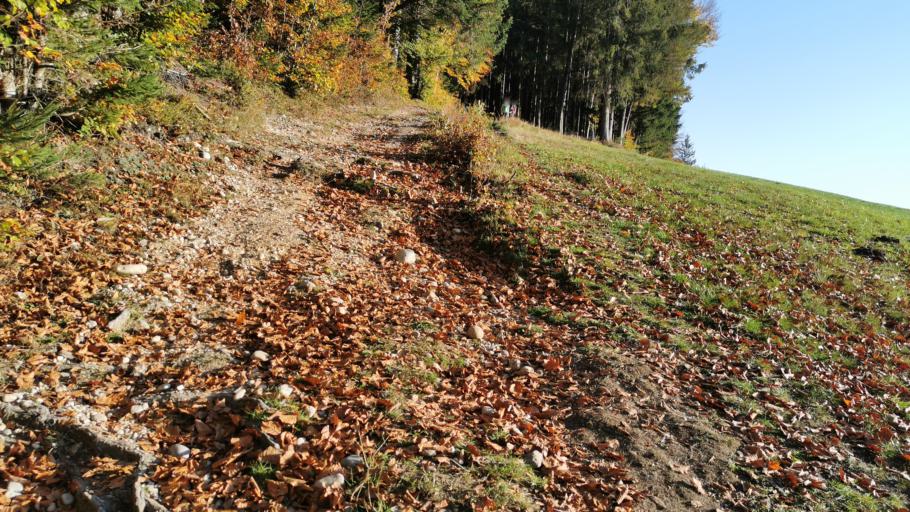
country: AT
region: Upper Austria
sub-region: Politischer Bezirk Vocklabruck
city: Frankenburg
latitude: 48.1028
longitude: 13.5205
